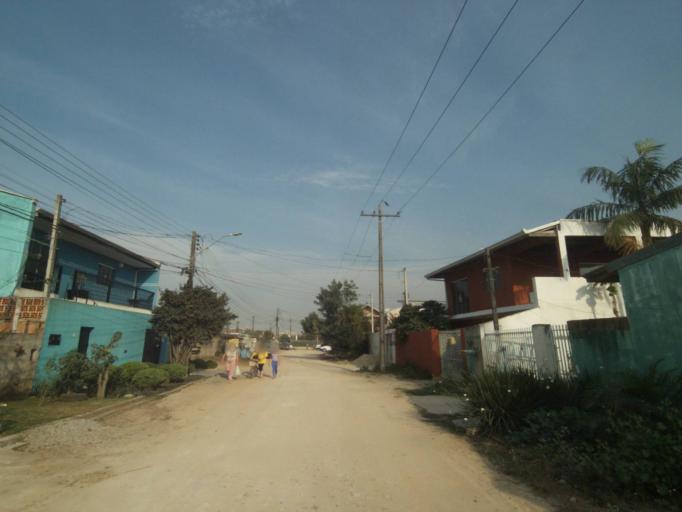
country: BR
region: Parana
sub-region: Sao Jose Dos Pinhais
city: Sao Jose dos Pinhais
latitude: -25.4971
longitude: -49.2073
